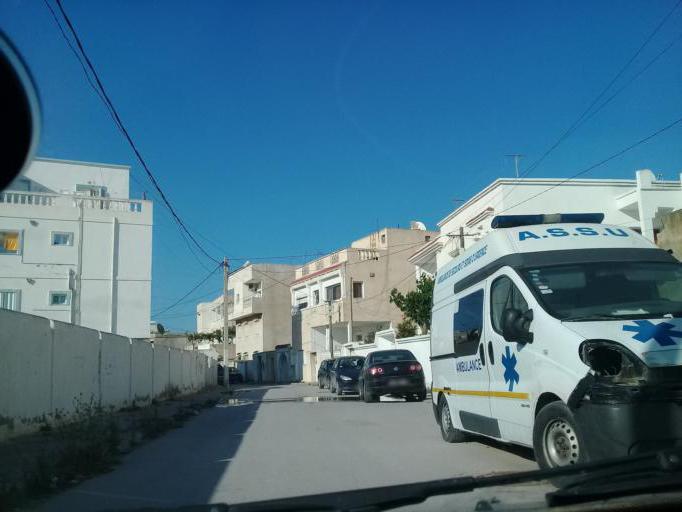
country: TN
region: Tunis
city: La Goulette
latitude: 36.8201
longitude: 10.3053
